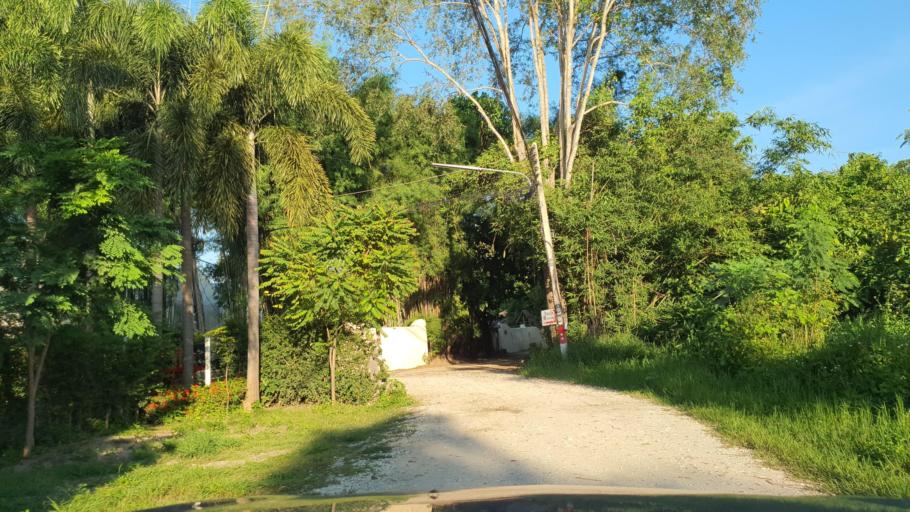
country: TH
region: Chiang Mai
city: Hang Dong
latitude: 18.6828
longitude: 98.8882
